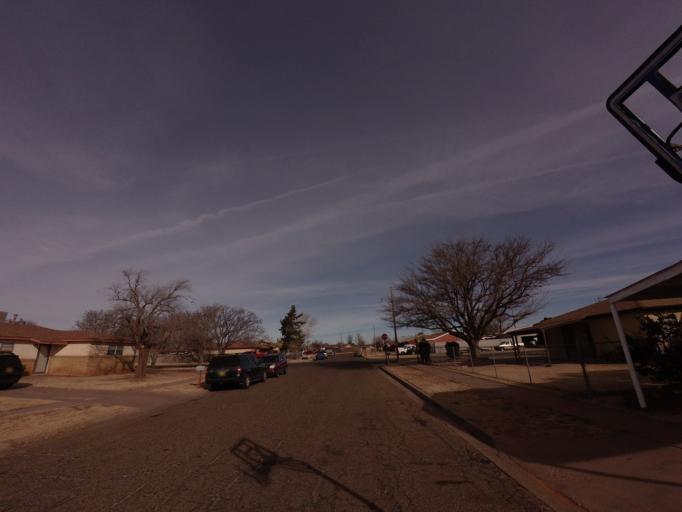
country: US
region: New Mexico
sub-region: Curry County
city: Clovis
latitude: 34.4153
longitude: -103.2200
